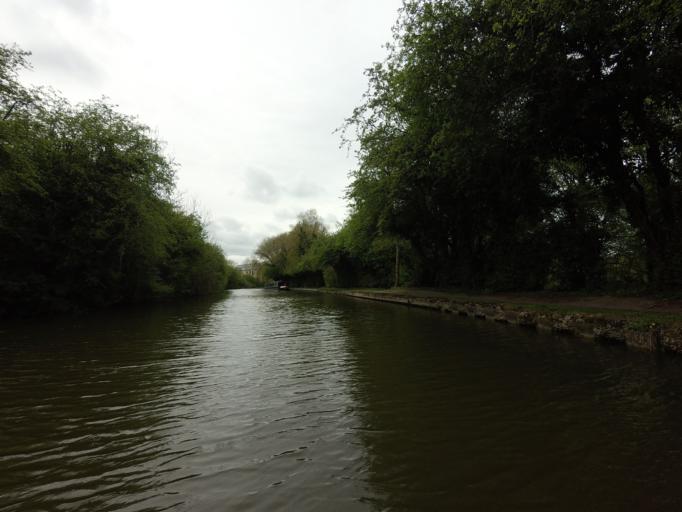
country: GB
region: England
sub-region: Milton Keynes
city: Simpson
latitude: 52.0266
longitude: -0.7265
